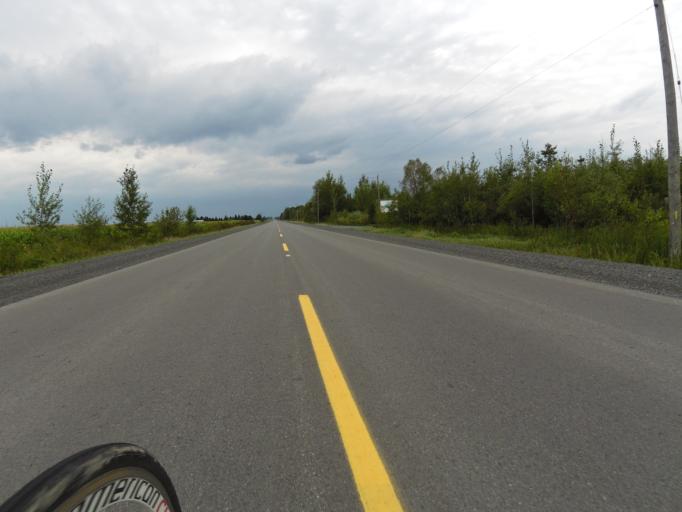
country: CA
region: Ontario
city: Bells Corners
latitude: 45.2067
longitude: -75.7665
